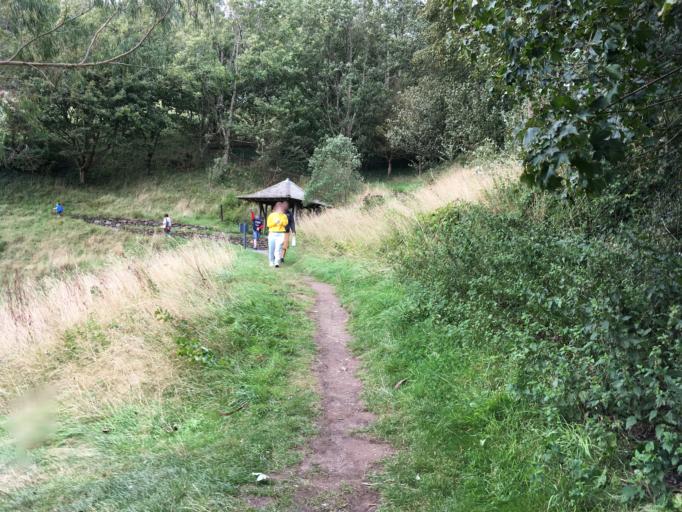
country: GB
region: England
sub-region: Devon
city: Dartmouth
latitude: 50.3464
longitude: -3.5305
